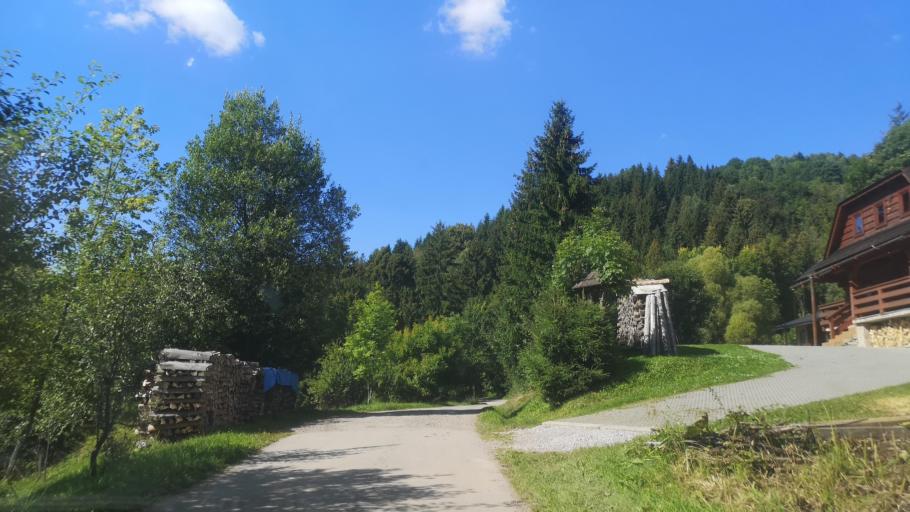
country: SK
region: Zilinsky
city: Oravska Lesna
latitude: 49.2943
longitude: 19.1395
